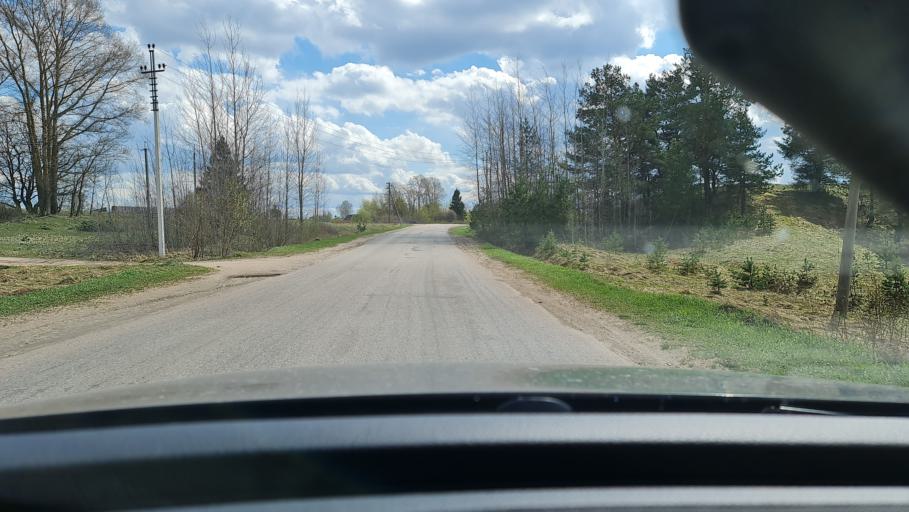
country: RU
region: Tverskaya
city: Toropets
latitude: 56.4809
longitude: 31.6340
